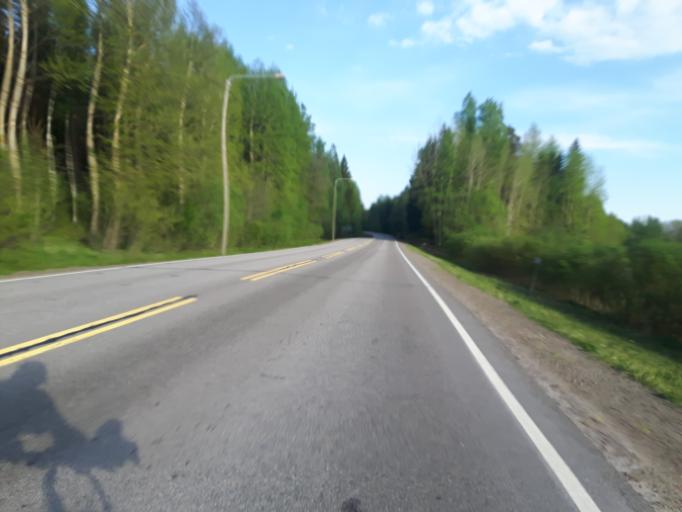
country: FI
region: Uusimaa
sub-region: Loviisa
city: Perna
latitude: 60.4630
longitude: 26.0393
